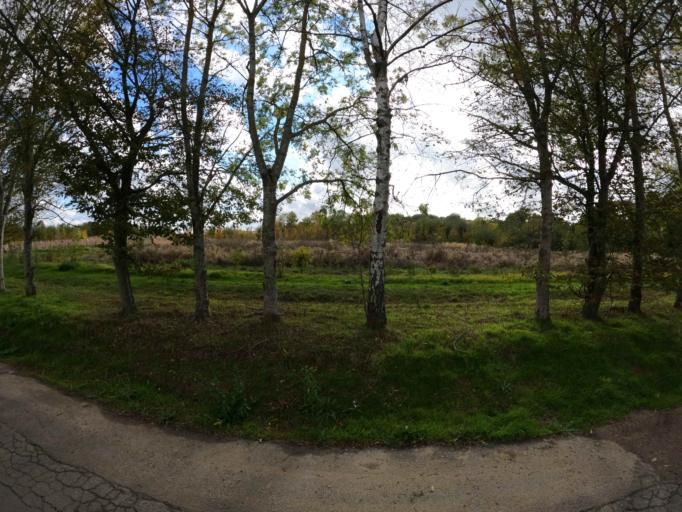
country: FR
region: Ile-de-France
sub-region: Departement de Seine-et-Marne
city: Coupvray
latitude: 48.8888
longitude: 2.8026
